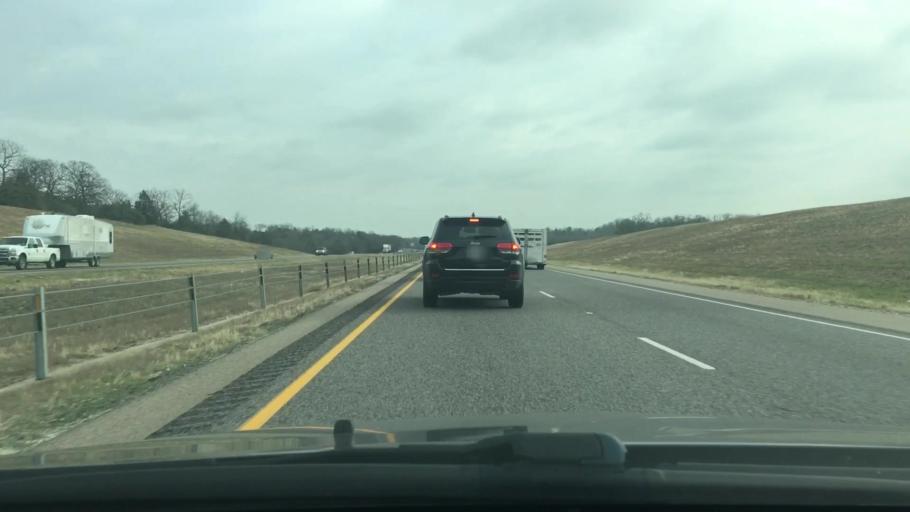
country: US
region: Texas
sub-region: Leon County
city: Buffalo
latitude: 31.5149
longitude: -96.1062
